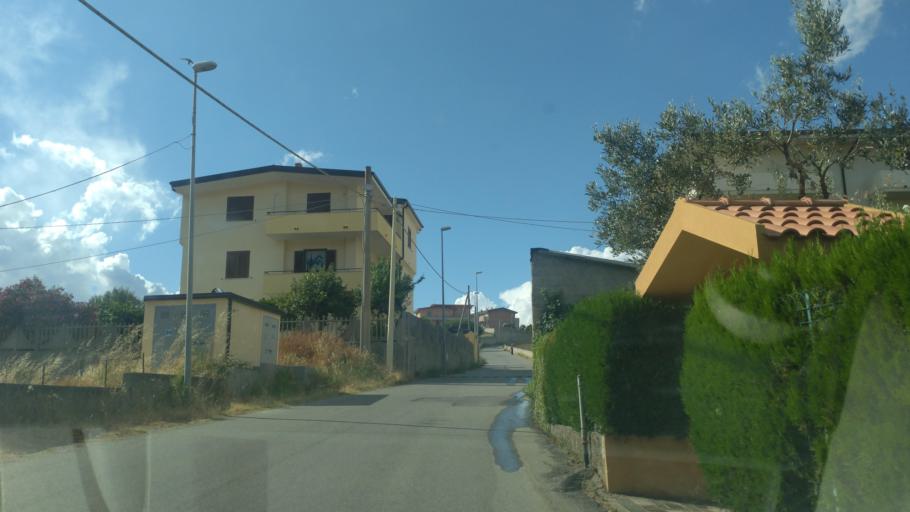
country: IT
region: Calabria
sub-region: Provincia di Catanzaro
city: Staletti
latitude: 38.7597
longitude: 16.5399
